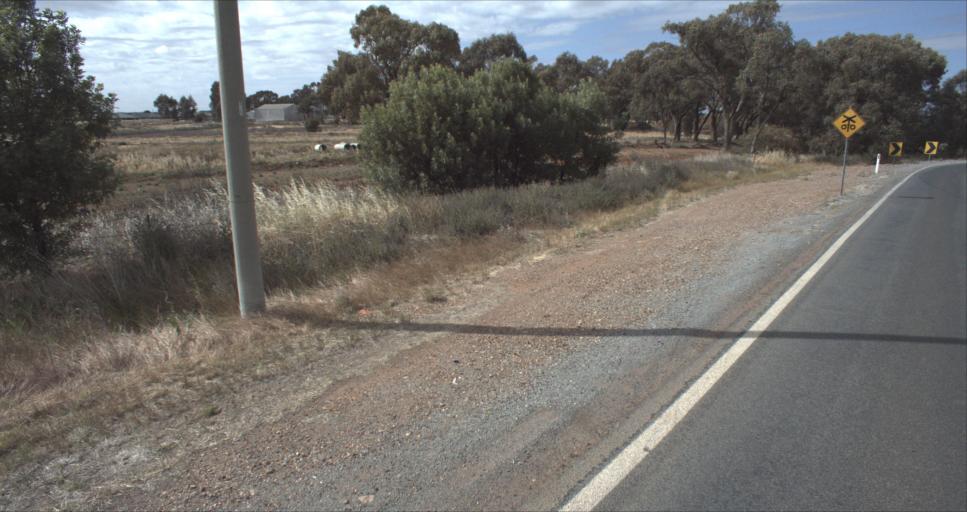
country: AU
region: New South Wales
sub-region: Leeton
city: Leeton
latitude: -34.5690
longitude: 146.3947
